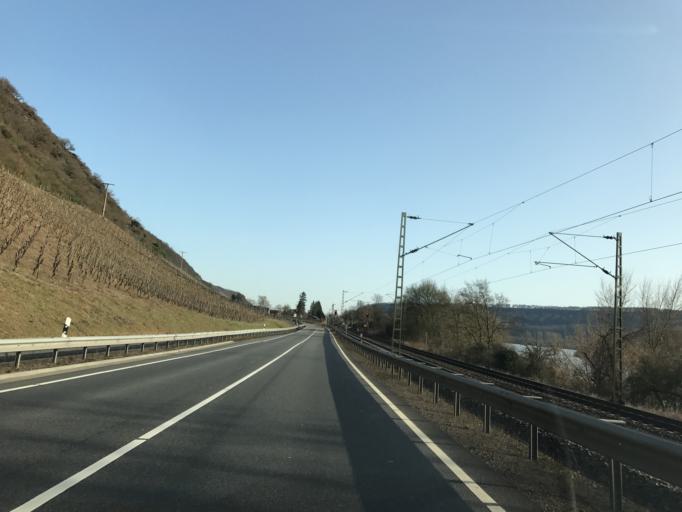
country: DE
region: Rheinland-Pfalz
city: Hammerstein
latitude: 50.4682
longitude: 7.3596
